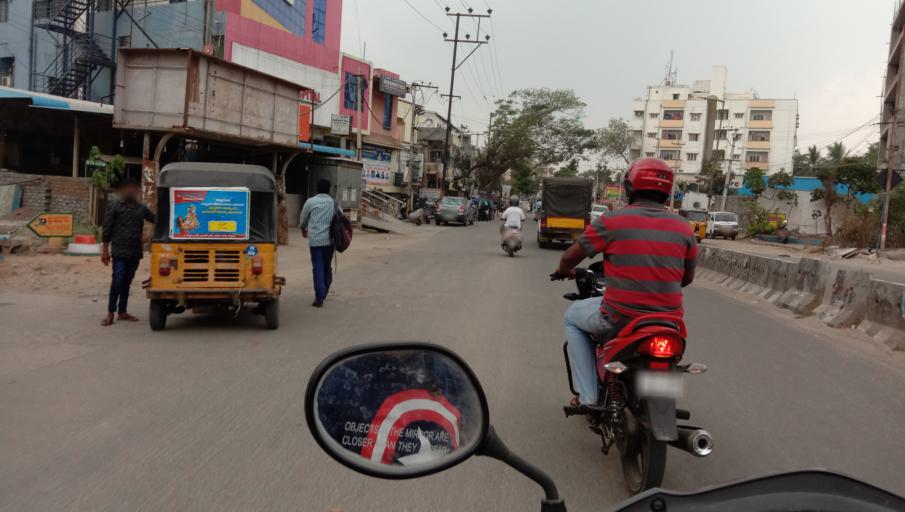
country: IN
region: Telangana
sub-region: Rangareddi
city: Lal Bahadur Nagar
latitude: 17.3763
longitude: 78.5572
